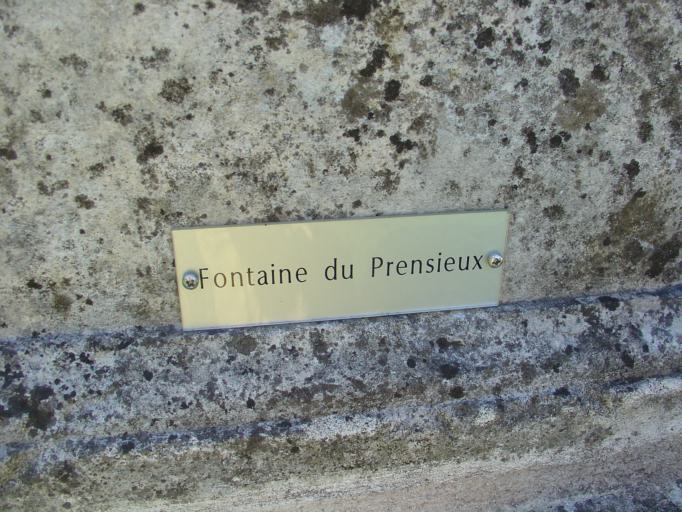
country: FR
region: Lorraine
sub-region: Departement de Meurthe-et-Moselle
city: Foug
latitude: 48.7067
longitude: 5.8063
